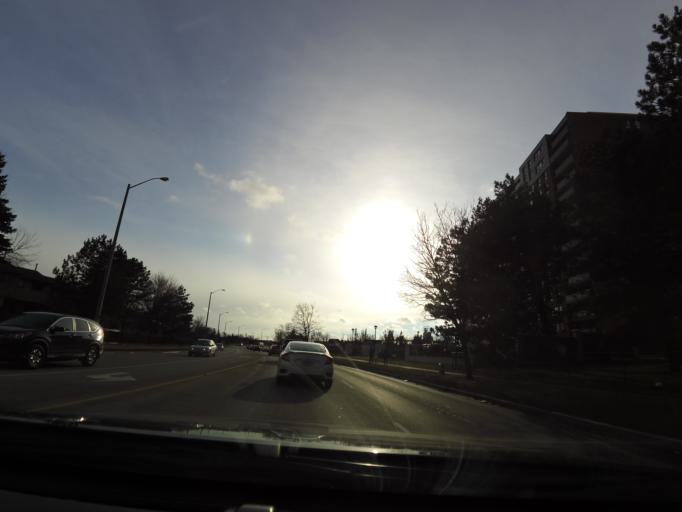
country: CA
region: Ontario
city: Brampton
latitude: 43.7091
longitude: -79.7244
